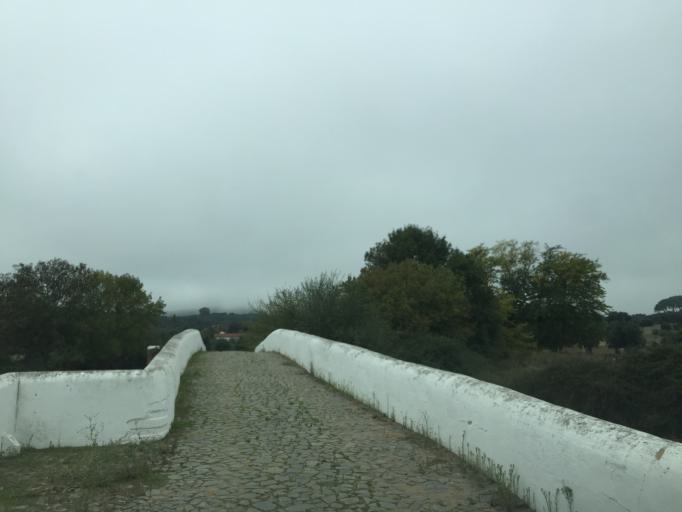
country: PT
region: Portalegre
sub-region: Arronches
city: Arronches
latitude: 39.0578
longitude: -7.4434
